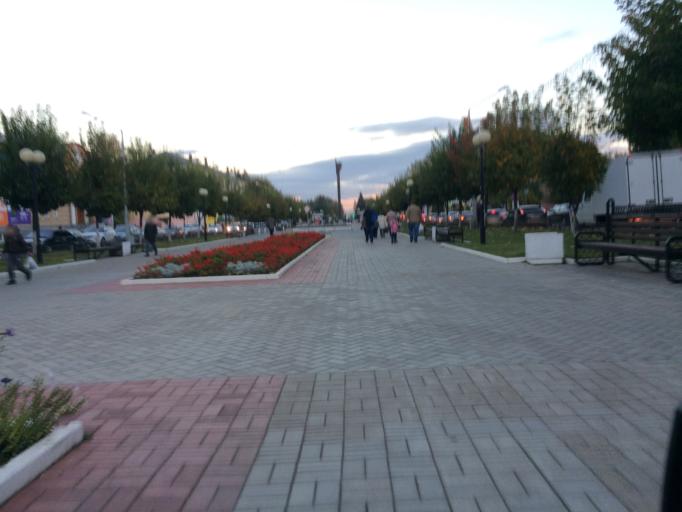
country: RU
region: Mariy-El
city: Yoshkar-Ola
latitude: 56.6379
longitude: 47.8832
